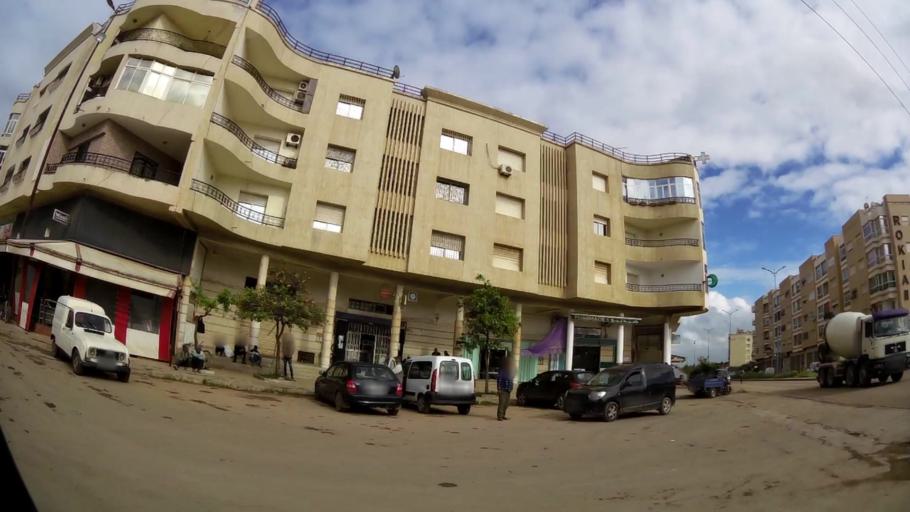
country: MA
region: Grand Casablanca
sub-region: Mohammedia
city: Mohammedia
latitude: 33.6845
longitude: -7.3724
